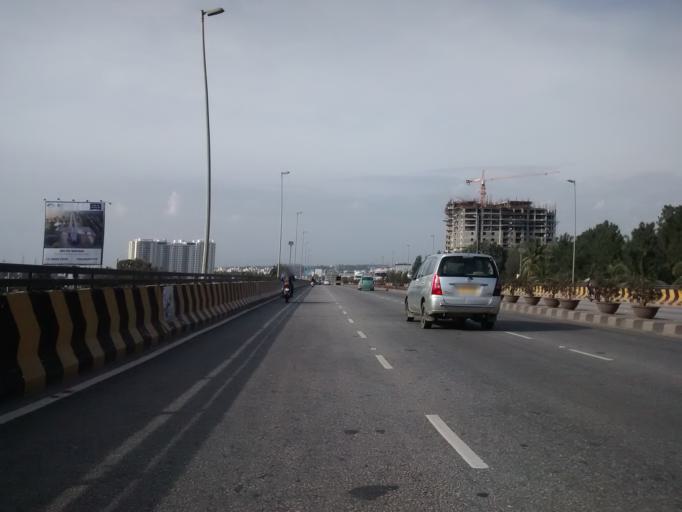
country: IN
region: Karnataka
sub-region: Bangalore Urban
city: Yelahanka
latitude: 13.0841
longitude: 77.5939
